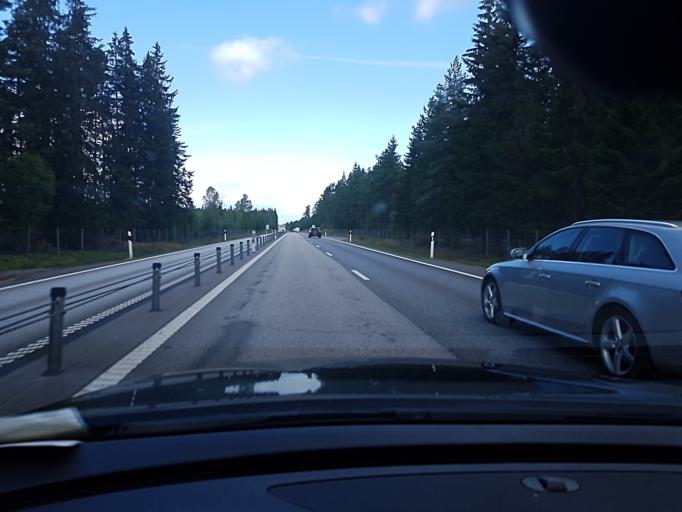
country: SE
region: Kronoberg
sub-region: Lessebo Kommun
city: Hovmantorp
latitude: 56.8232
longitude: 15.0893
